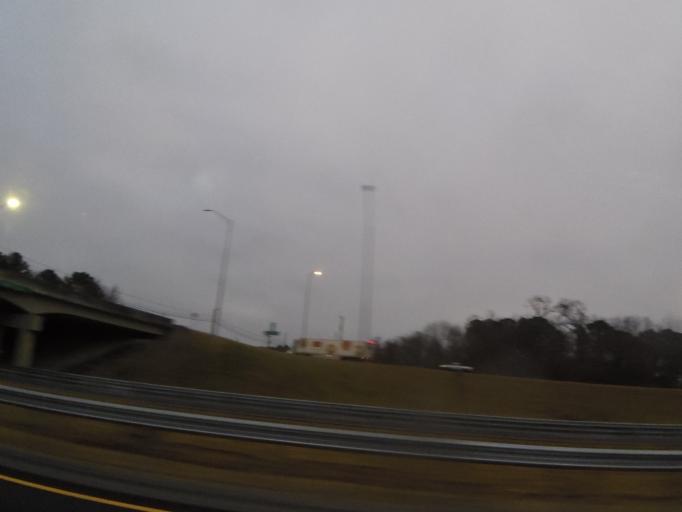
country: US
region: Alabama
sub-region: Cullman County
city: Cullman
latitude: 34.1702
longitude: -86.8753
